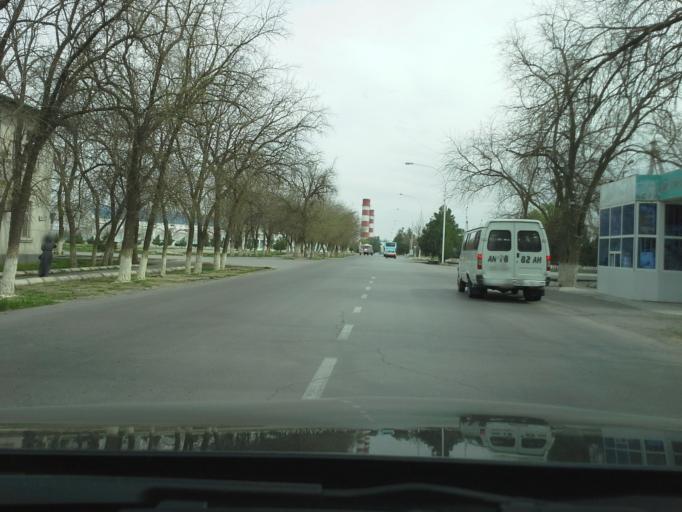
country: TM
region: Ahal
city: Abadan
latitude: 38.0604
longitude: 58.1570
